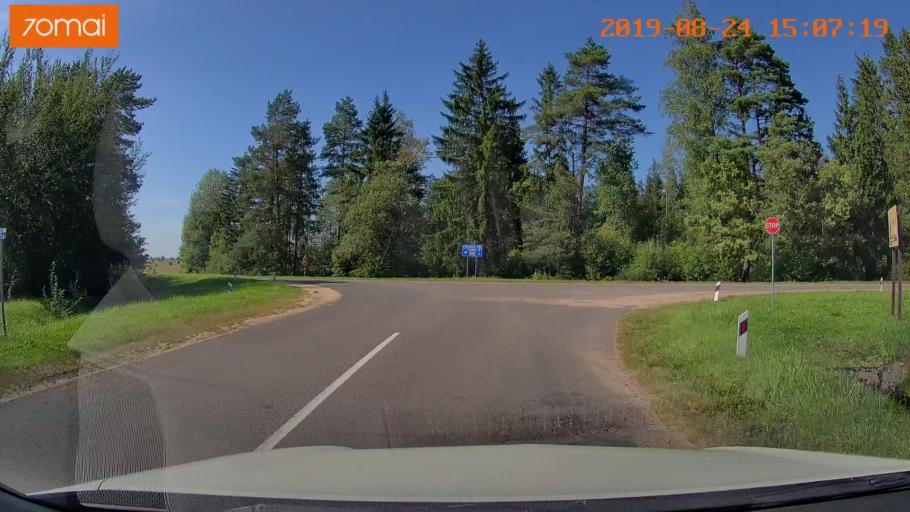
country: BY
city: Michanovichi
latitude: 53.6082
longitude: 27.6741
